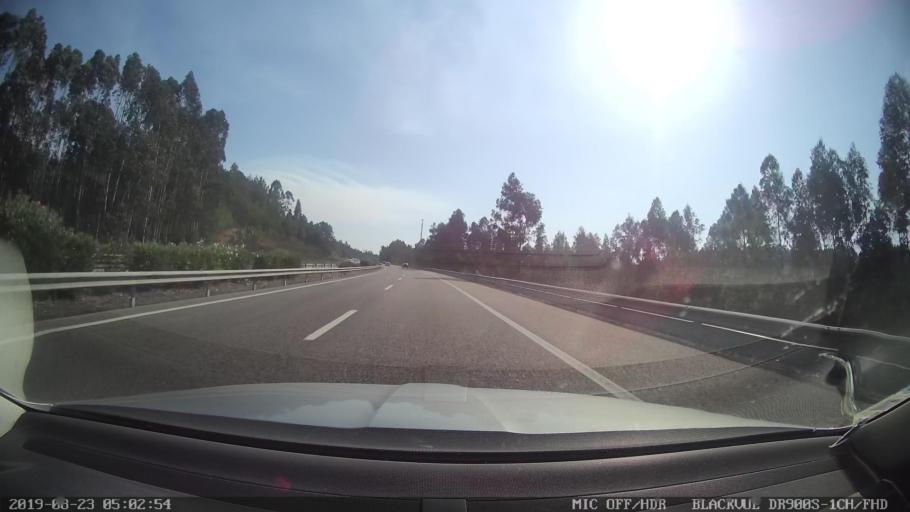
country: PT
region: Leiria
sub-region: Pombal
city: Pombal
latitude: 39.9662
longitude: -8.6588
